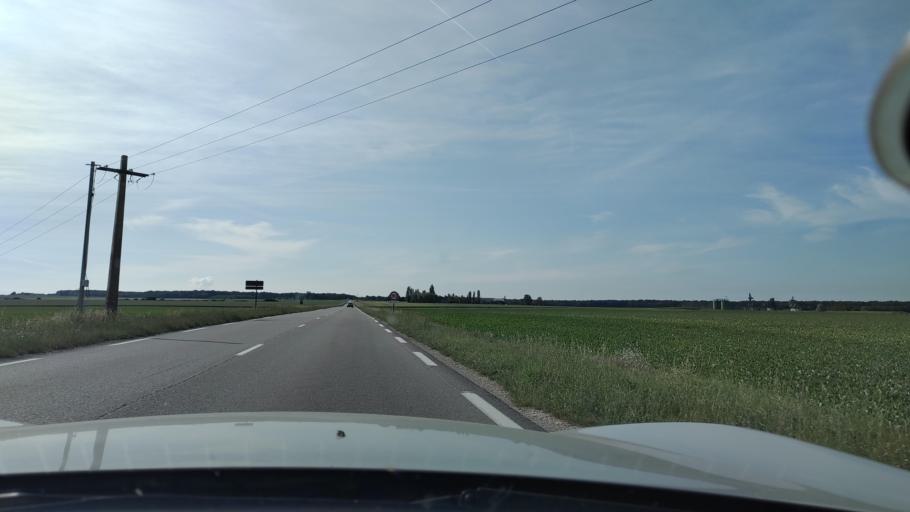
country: FR
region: Ile-de-France
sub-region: Departement de Seine-et-Marne
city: Jouy-le-Chatel
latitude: 48.6553
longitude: 3.1501
